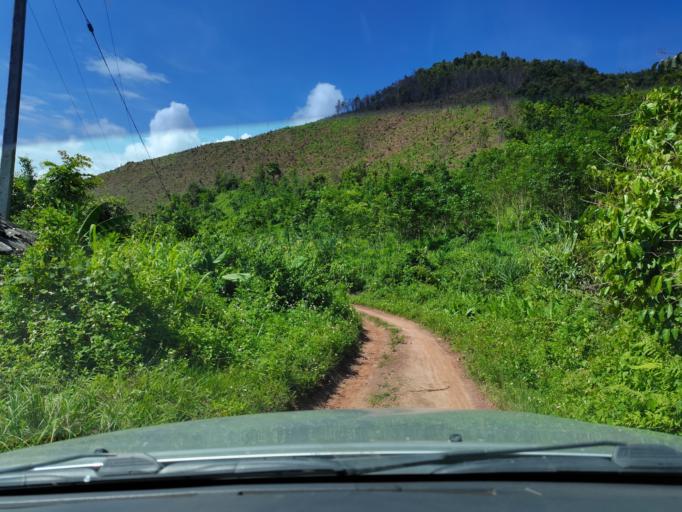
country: LA
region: Loungnamtha
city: Muang Nale
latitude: 20.5534
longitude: 101.0655
